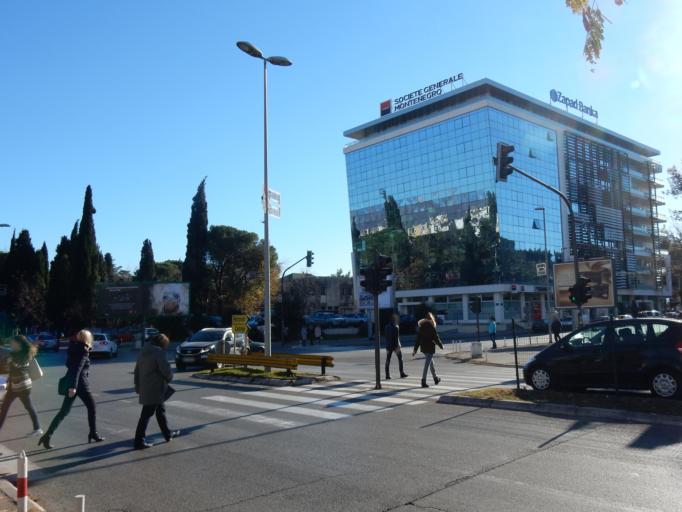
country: ME
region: Podgorica
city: Podgorica
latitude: 42.4411
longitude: 19.2472
